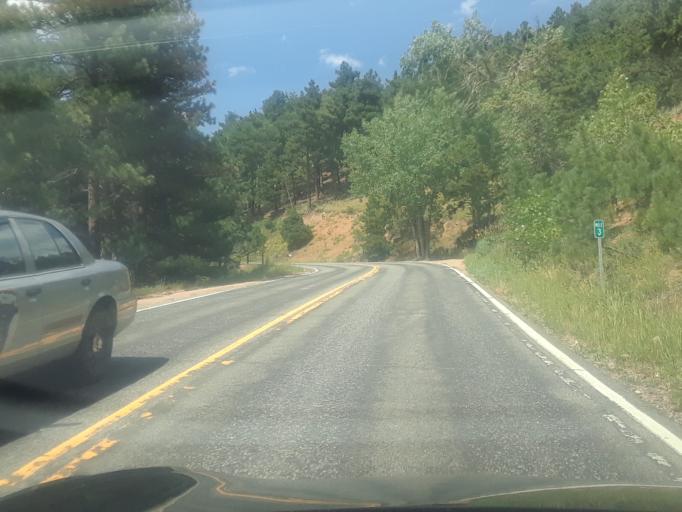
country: US
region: Colorado
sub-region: Boulder County
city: Boulder
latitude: 40.0381
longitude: -105.3280
